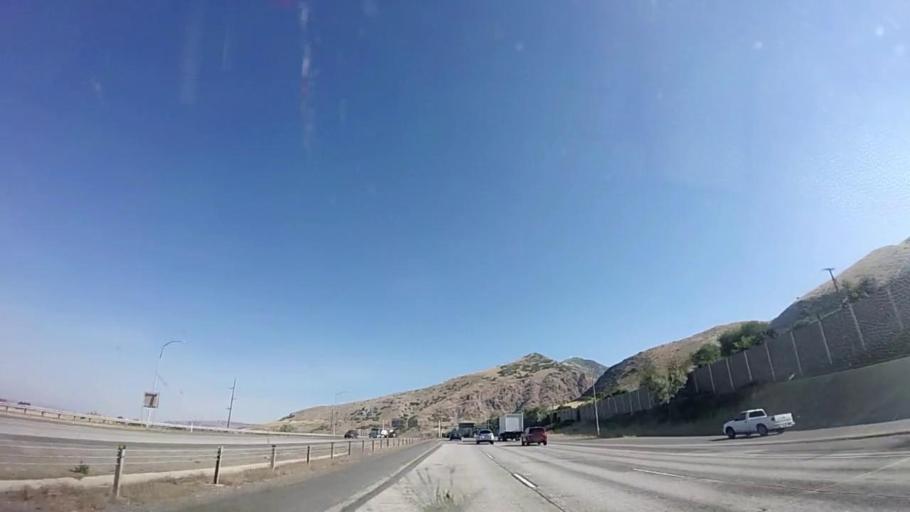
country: US
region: Utah
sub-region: Salt Lake County
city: East Millcreek
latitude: 40.7012
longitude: -111.7951
